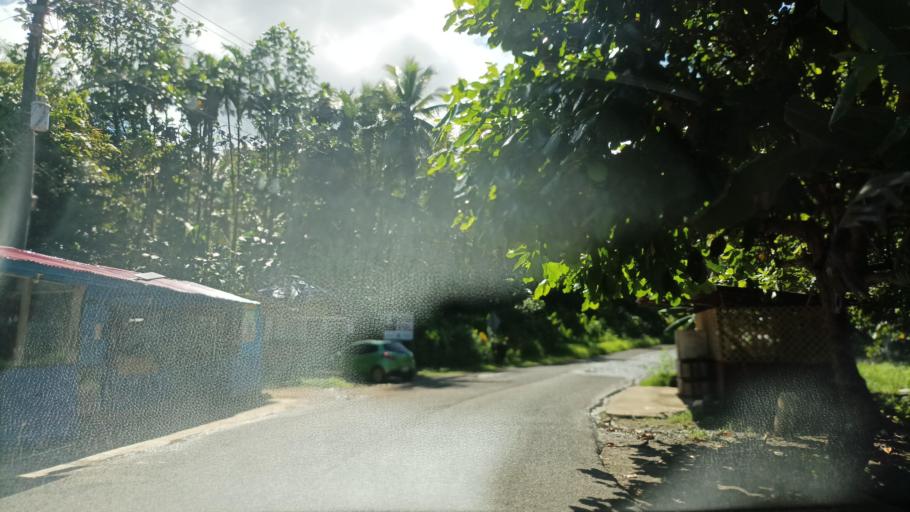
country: FM
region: Pohnpei
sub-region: Madolenihm Municipality
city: Madolenihm Municipality Government
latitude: 6.8465
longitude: 158.3020
